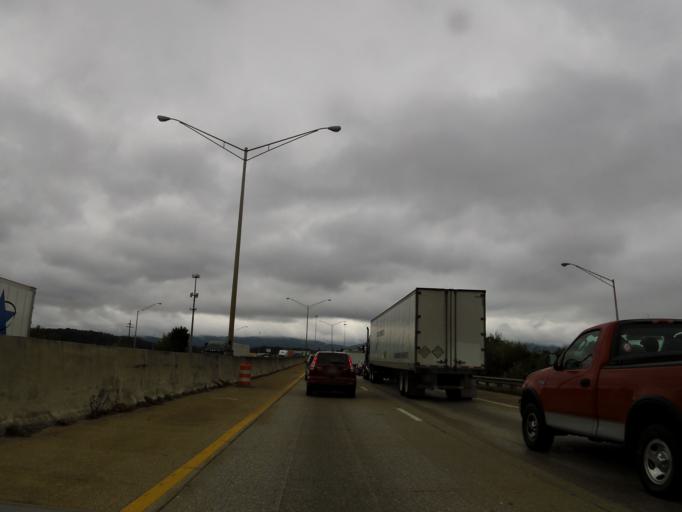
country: US
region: Tennessee
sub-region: Hamilton County
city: Chattanooga
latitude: 35.0301
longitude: -85.3134
